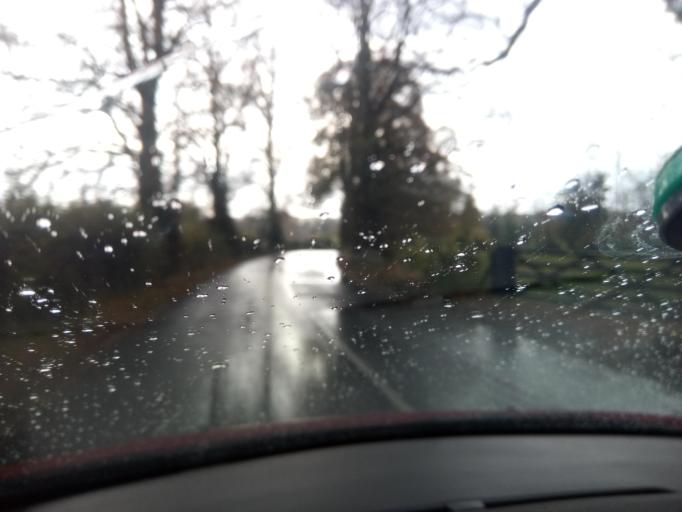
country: GB
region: England
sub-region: Northumberland
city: Birtley
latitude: 55.0973
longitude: -2.2237
